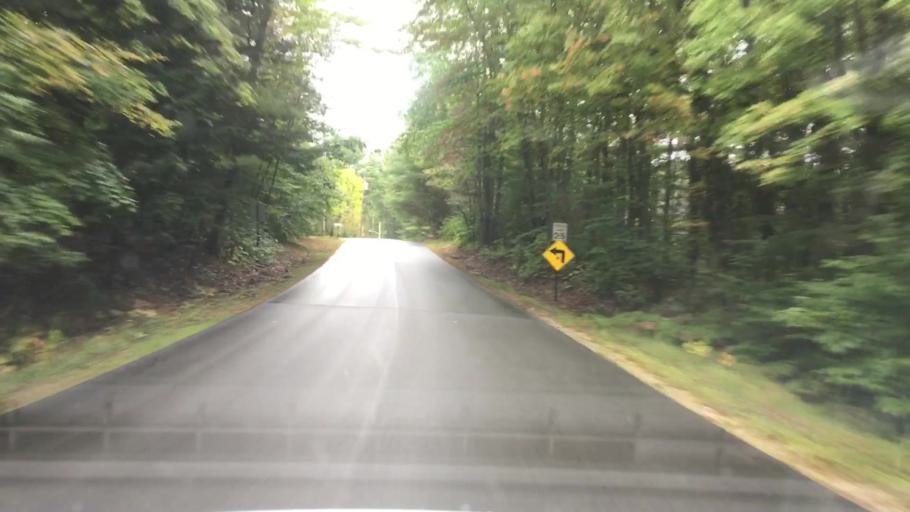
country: US
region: Maine
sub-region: Cumberland County
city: Raymond
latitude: 43.9975
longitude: -70.5679
